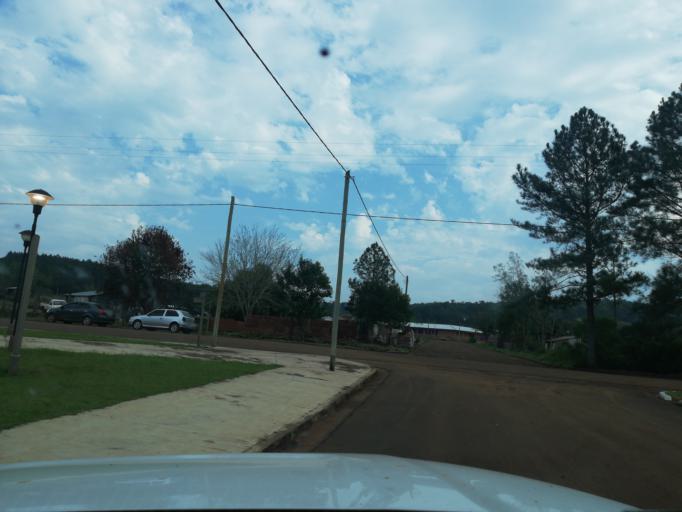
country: AR
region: Misiones
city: Cerro Azul
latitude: -27.5696
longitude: -55.5025
